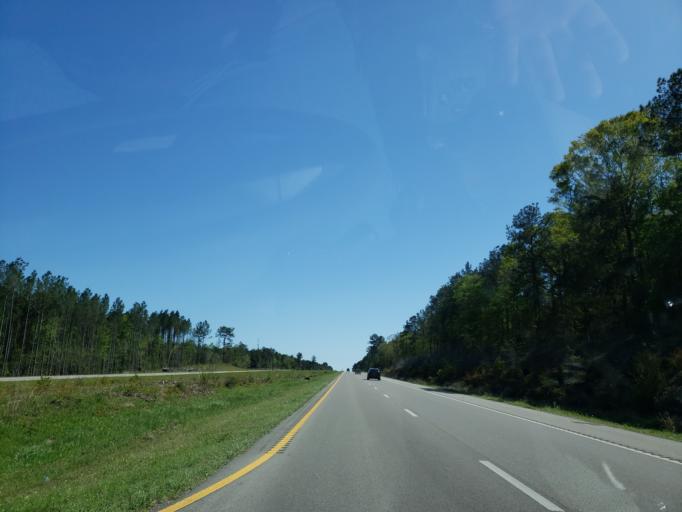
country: US
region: Mississippi
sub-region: Stone County
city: Wiggins
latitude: 31.0421
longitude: -89.2025
